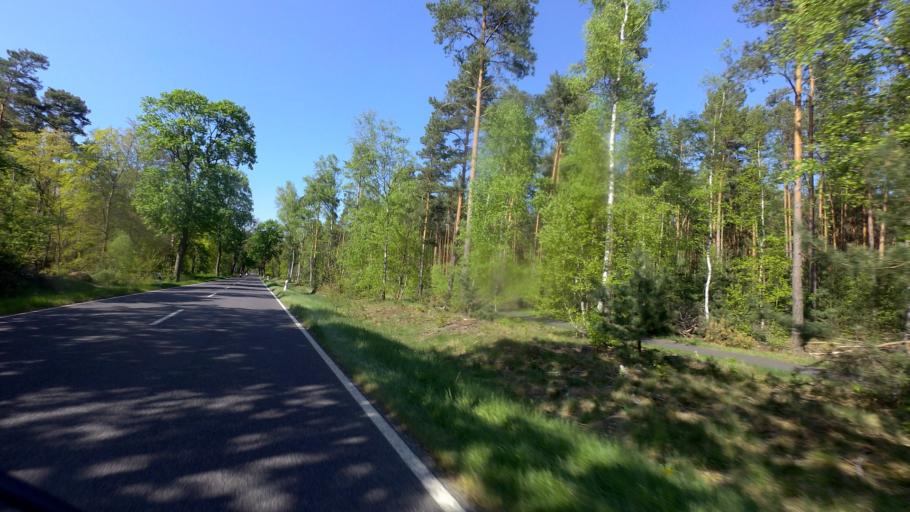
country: DE
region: Brandenburg
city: Halbe
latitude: 52.1446
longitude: 13.7470
